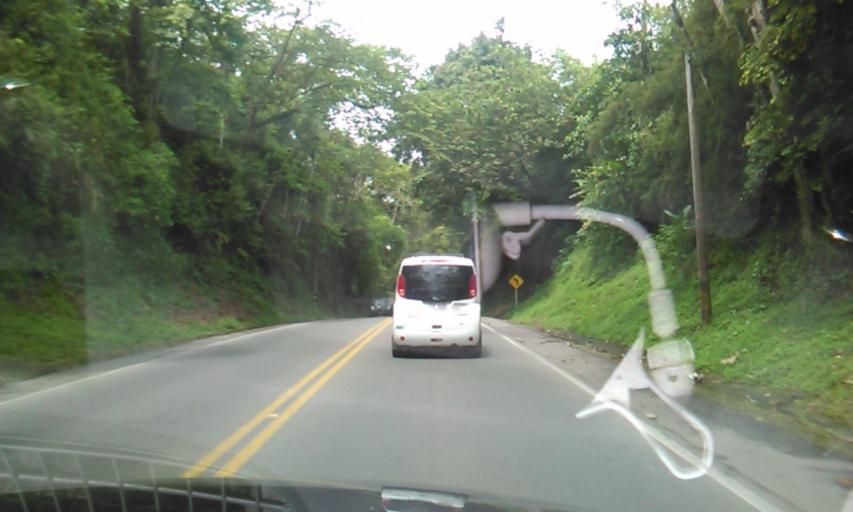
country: CO
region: Quindio
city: Montenegro
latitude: 4.5523
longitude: -75.7443
